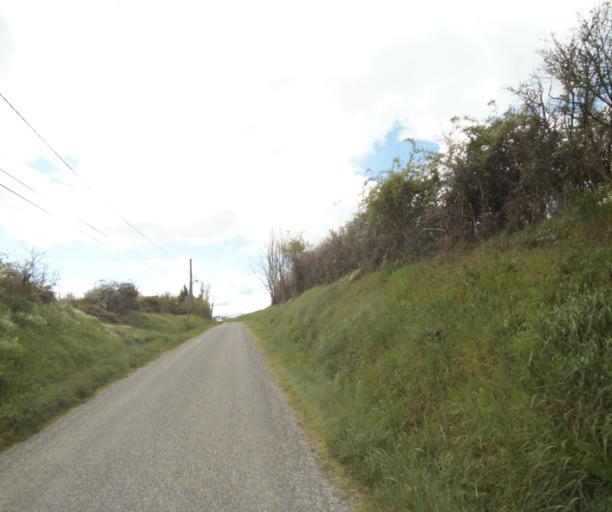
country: FR
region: Midi-Pyrenees
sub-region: Departement de l'Ariege
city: Saverdun
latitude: 43.2253
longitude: 1.5783
